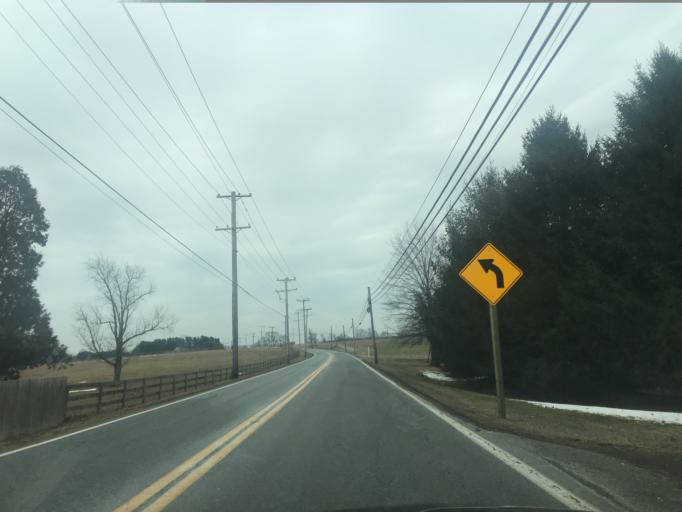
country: US
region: Maryland
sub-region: Harford County
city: Jarrettsville
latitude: 39.6154
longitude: -76.5411
